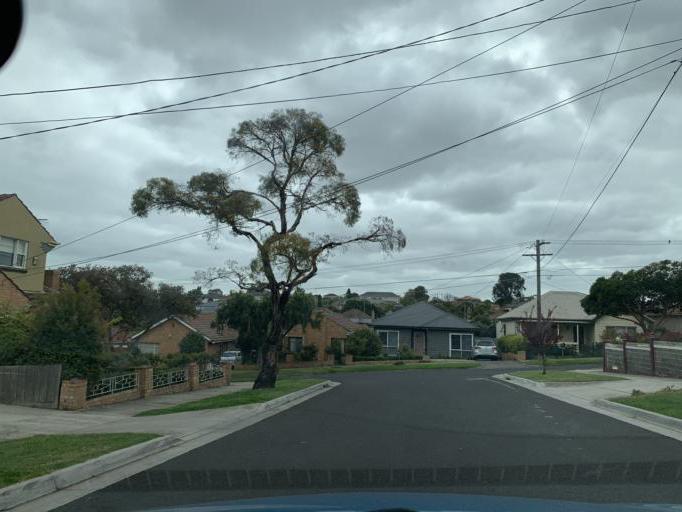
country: AU
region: Victoria
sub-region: Moreland
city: Pascoe Vale South
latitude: -37.7472
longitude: 144.9399
